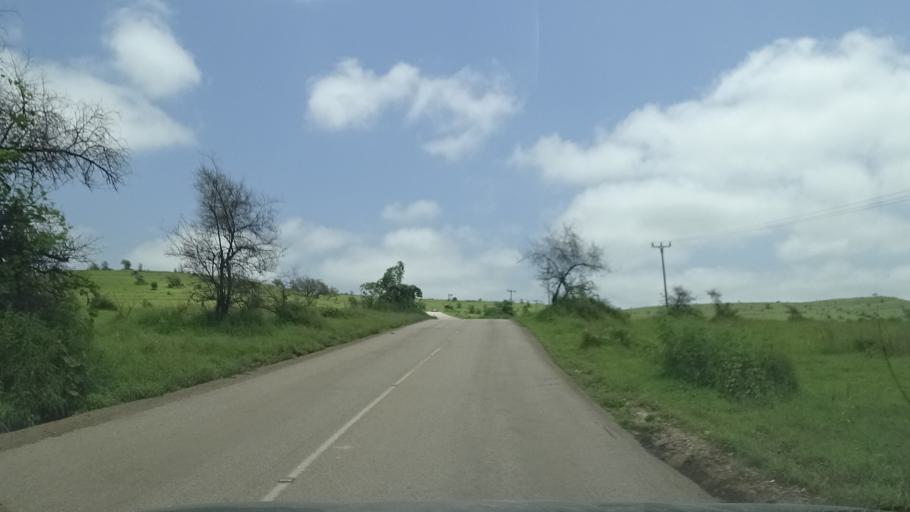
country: OM
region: Zufar
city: Salalah
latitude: 17.2036
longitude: 54.1857
